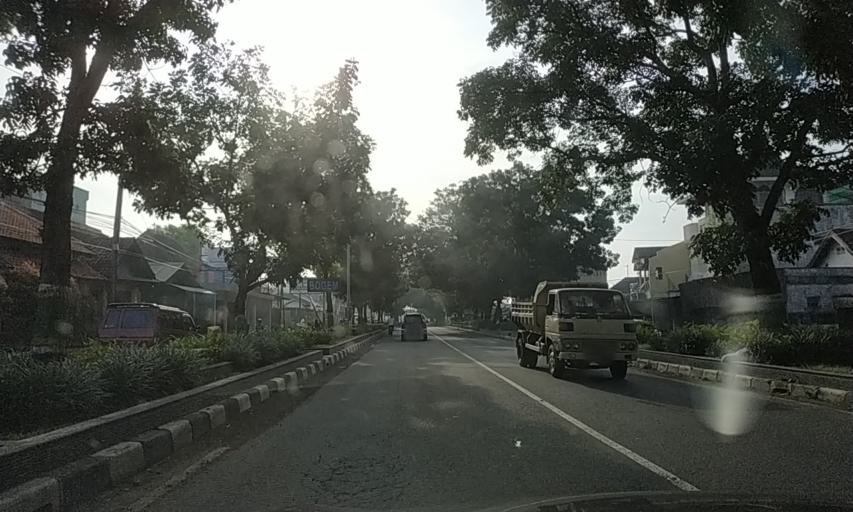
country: ID
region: Central Java
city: Candi Prambanan
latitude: -7.7562
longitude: 110.4851
